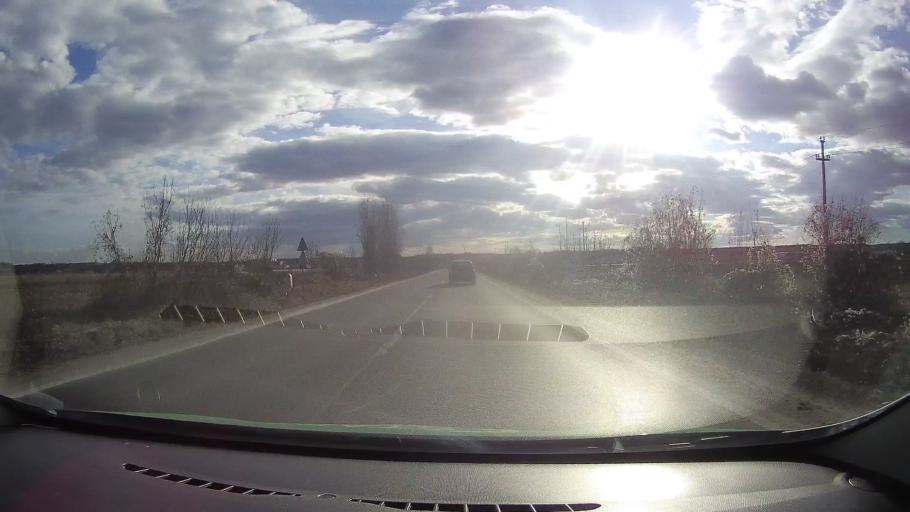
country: RO
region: Dambovita
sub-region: Comuna Lucieni
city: Lucieni
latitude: 44.8617
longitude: 25.4141
